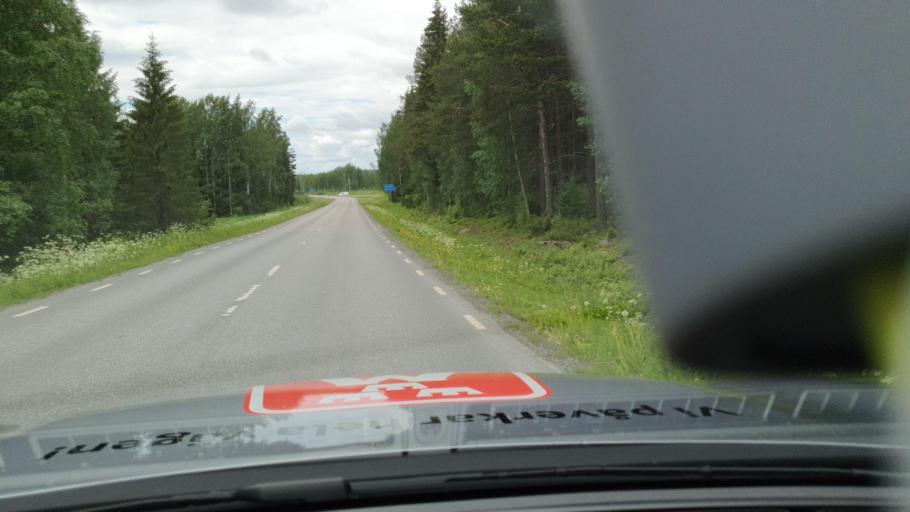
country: SE
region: Norrbotten
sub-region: Lulea Kommun
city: Sodra Sunderbyn
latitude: 65.8313
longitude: 21.9626
